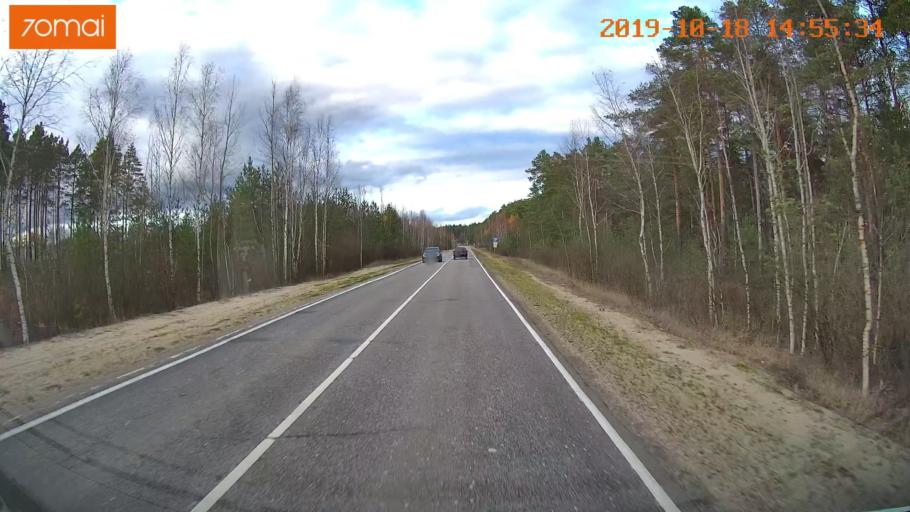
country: RU
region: Vladimir
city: Kurlovo
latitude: 55.4540
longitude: 40.5891
